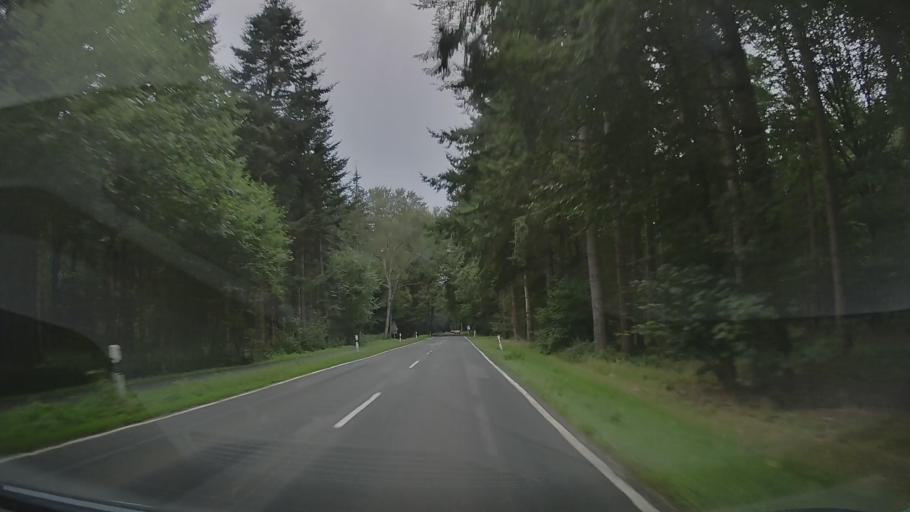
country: DE
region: Lower Saxony
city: Syke
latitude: 52.9099
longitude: 8.8594
